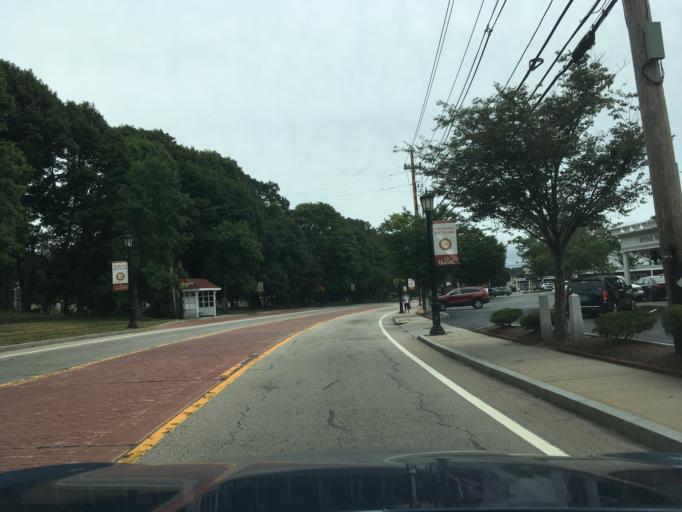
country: US
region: Rhode Island
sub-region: Bristol County
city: Barrington
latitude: 41.7422
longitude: -71.3108
